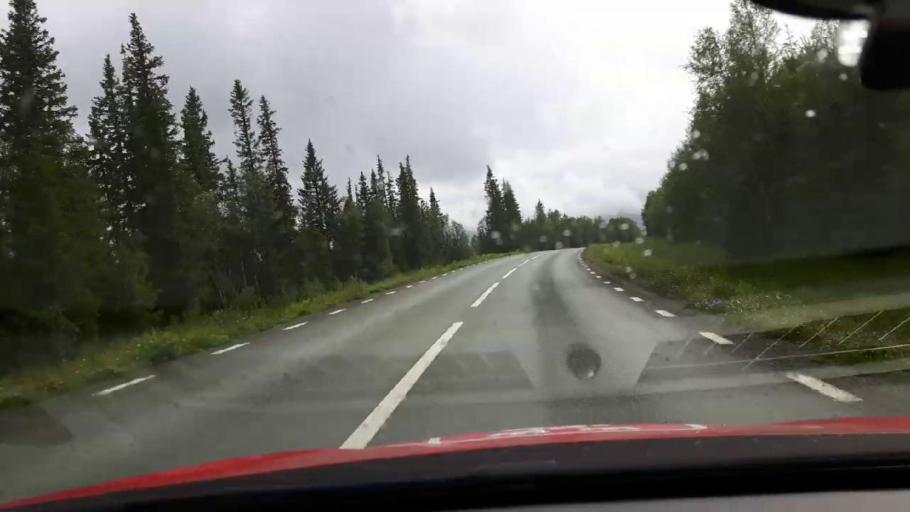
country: SE
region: Jaemtland
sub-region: Are Kommun
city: Are
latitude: 63.3015
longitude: 12.4215
